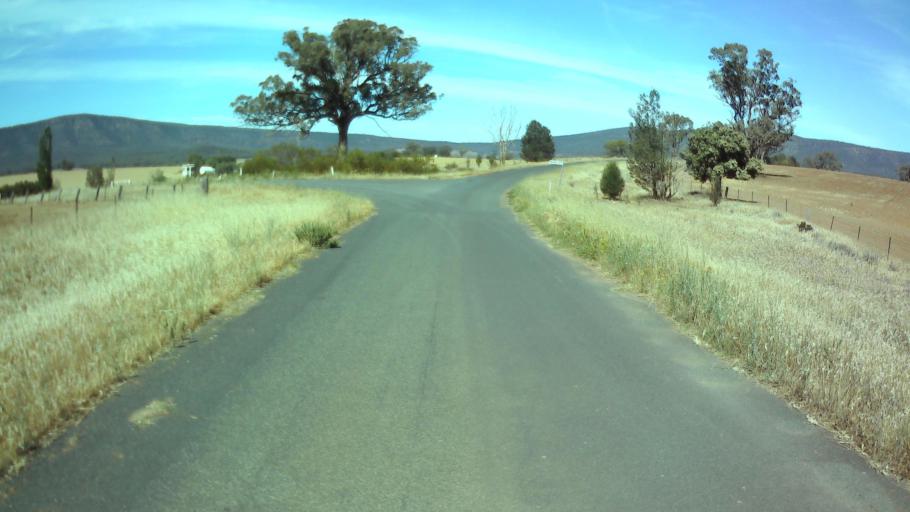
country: AU
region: New South Wales
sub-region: Weddin
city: Grenfell
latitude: -33.9408
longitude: 148.0680
